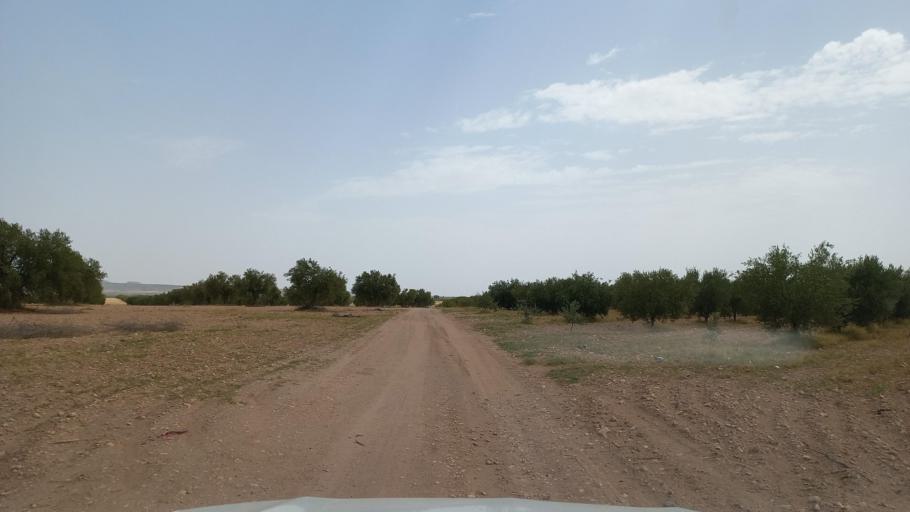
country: TN
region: Al Qasrayn
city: Kasserine
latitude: 35.2901
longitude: 9.0234
